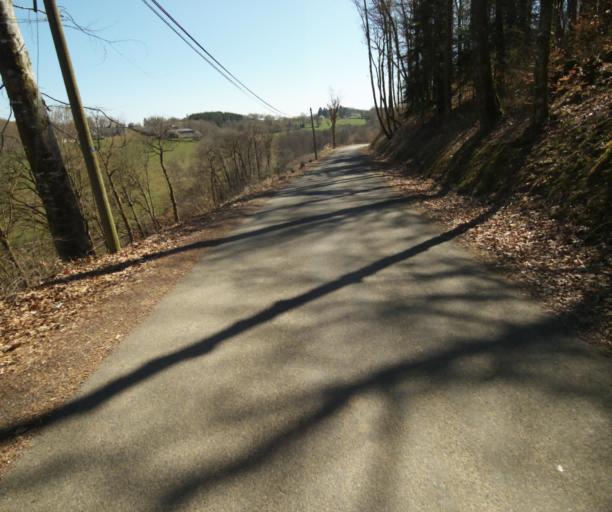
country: FR
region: Limousin
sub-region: Departement de la Correze
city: Saint-Clement
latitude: 45.3285
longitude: 1.7009
